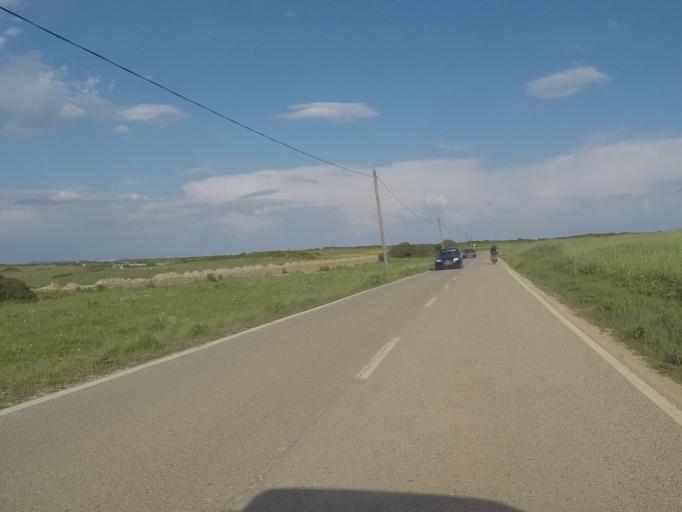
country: PT
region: Setubal
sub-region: Sesimbra
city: Sesimbra
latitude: 38.4201
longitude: -9.2080
